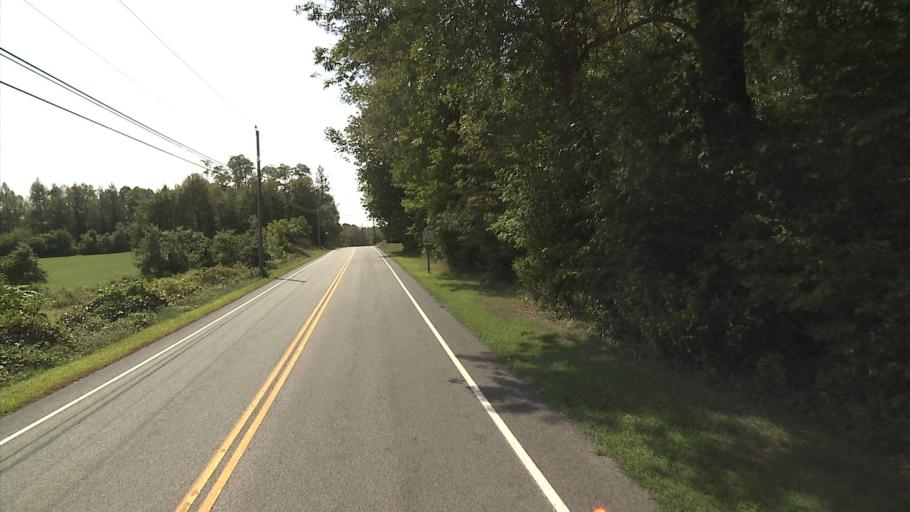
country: US
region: Connecticut
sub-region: Windham County
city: Plainfield Village
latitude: 41.7195
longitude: -71.9706
